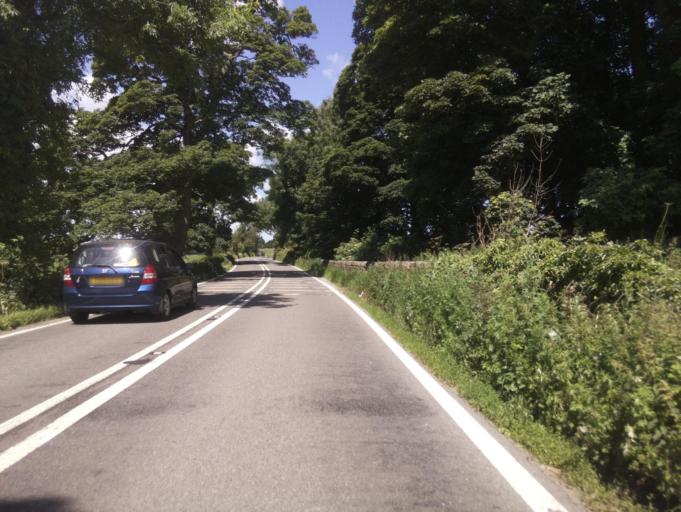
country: GB
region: England
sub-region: Derbyshire
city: Ashbourne
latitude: 53.0663
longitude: -1.7477
